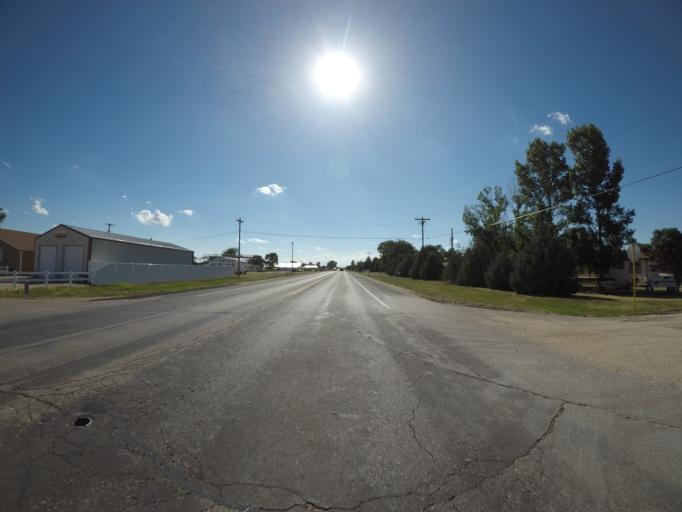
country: US
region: Colorado
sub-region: Logan County
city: Sterling
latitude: 40.6239
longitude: -103.2964
